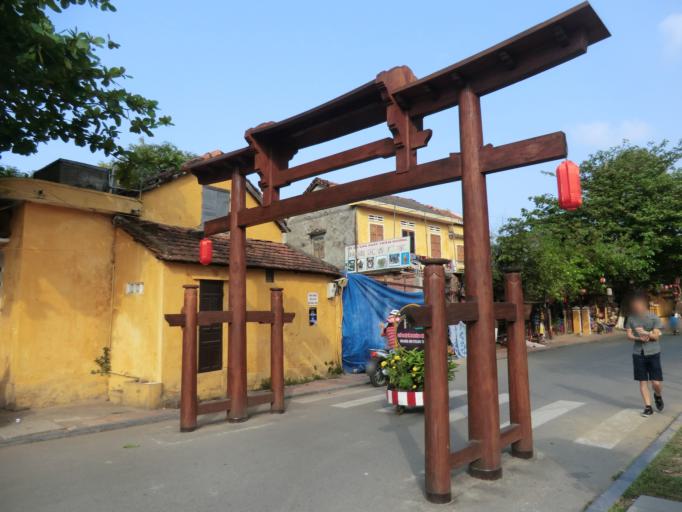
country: VN
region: Quang Nam
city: Hoi An
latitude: 15.8784
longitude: 108.3234
